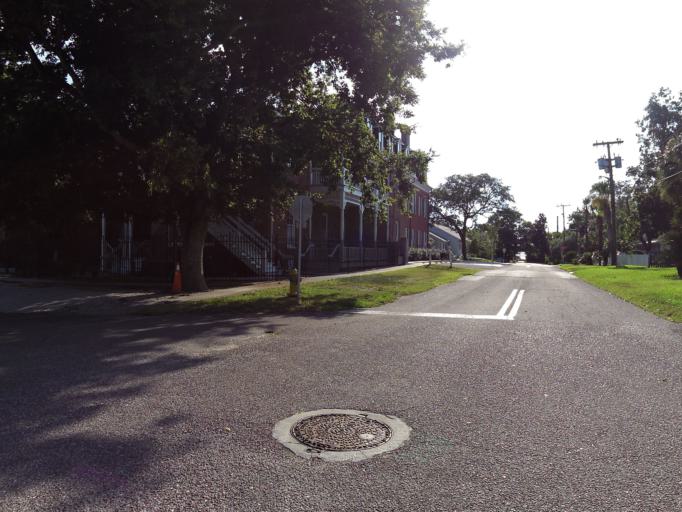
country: US
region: Florida
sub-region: Nassau County
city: Fernandina Beach
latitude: 30.6748
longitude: -81.4607
